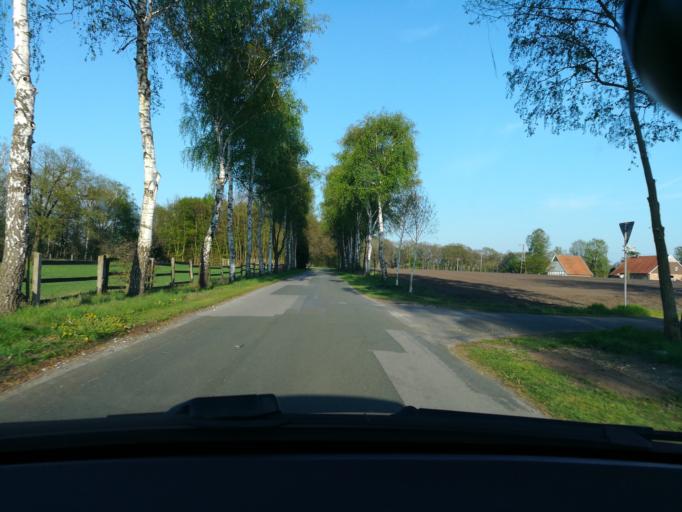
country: DE
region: North Rhine-Westphalia
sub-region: Regierungsbezirk Munster
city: Sassenberg
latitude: 52.0272
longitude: 8.0903
